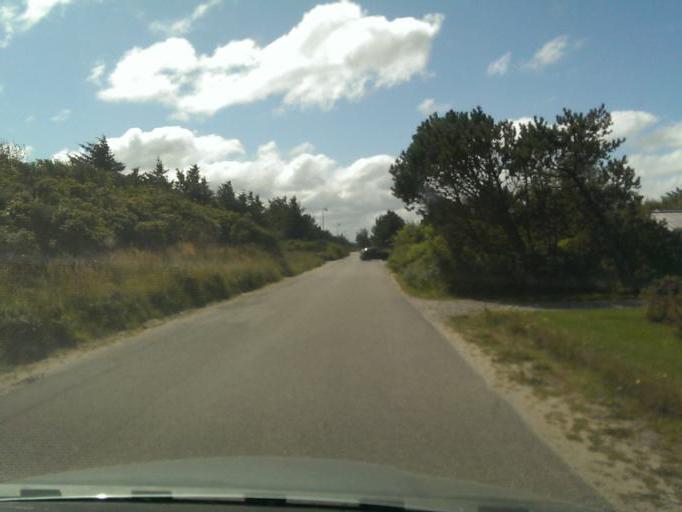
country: DK
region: North Denmark
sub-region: Jammerbugt Kommune
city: Pandrup
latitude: 57.2543
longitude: 9.5937
